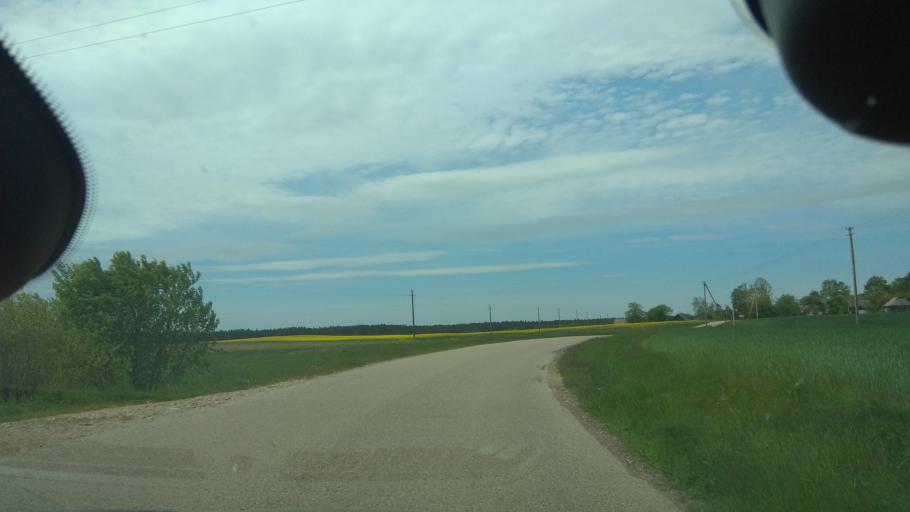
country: LT
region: Vilnius County
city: Ukmerge
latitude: 55.1607
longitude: 24.5235
